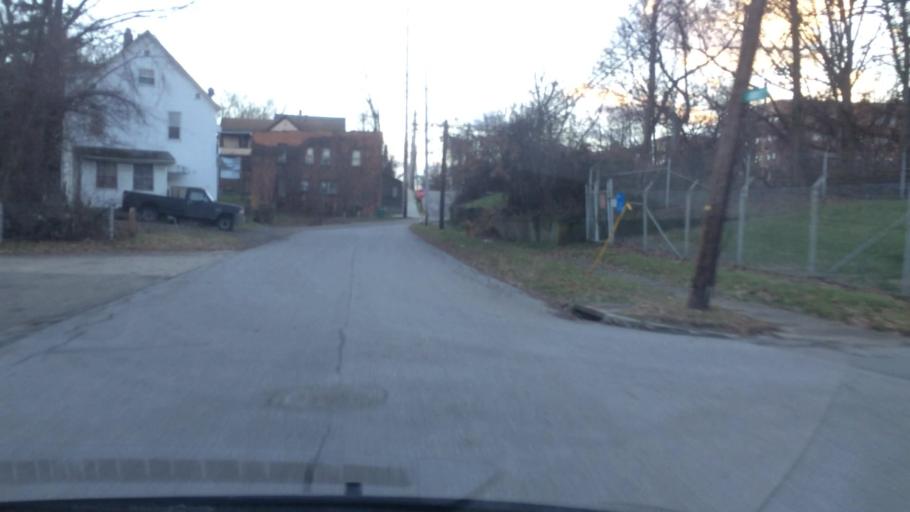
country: US
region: Ohio
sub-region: Summit County
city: Akron
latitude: 41.0840
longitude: -81.4981
